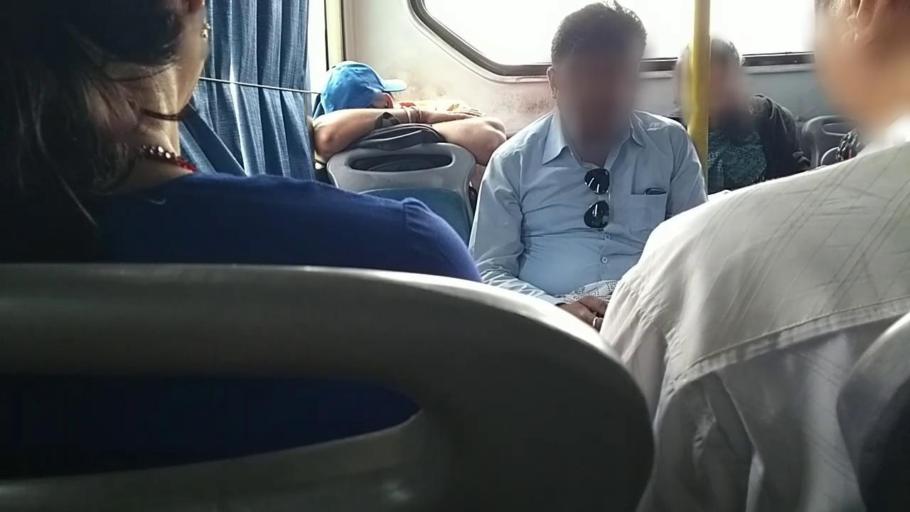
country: IN
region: Chhattisgarh
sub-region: Durg
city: Bhilai
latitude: 21.2084
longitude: 81.3666
